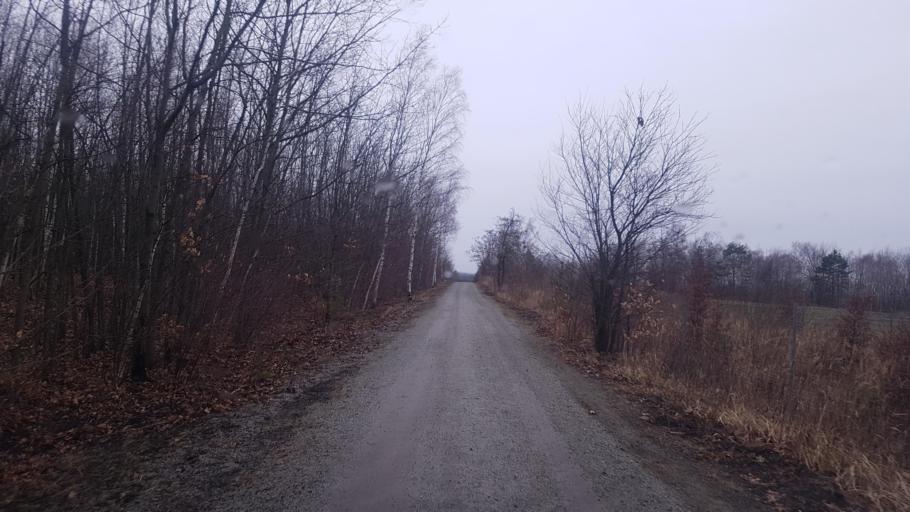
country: DE
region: Brandenburg
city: Schwarzheide
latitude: 51.4932
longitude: 13.8404
